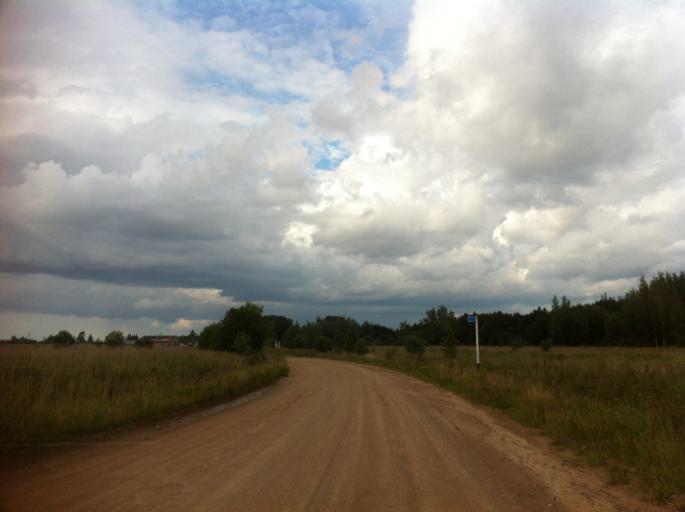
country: RU
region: Pskov
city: Izborsk
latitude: 57.8337
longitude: 27.9849
